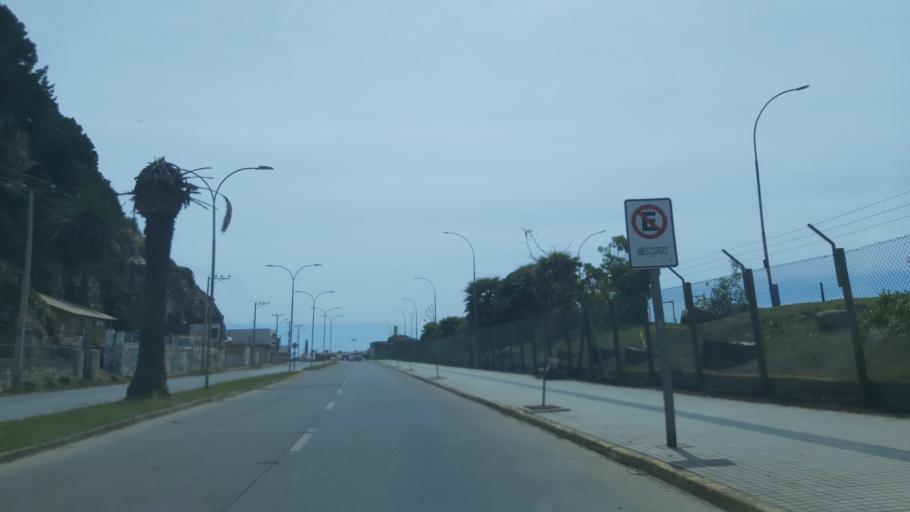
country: CL
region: Maule
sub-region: Provincia de Talca
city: Constitucion
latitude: -35.3267
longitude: -72.4223
